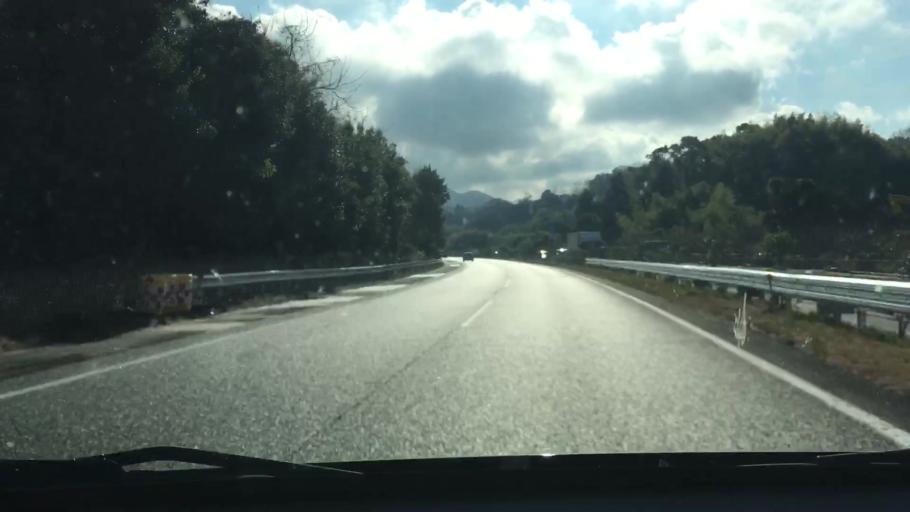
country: JP
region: Kumamoto
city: Matsubase
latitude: 32.5600
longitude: 130.6969
